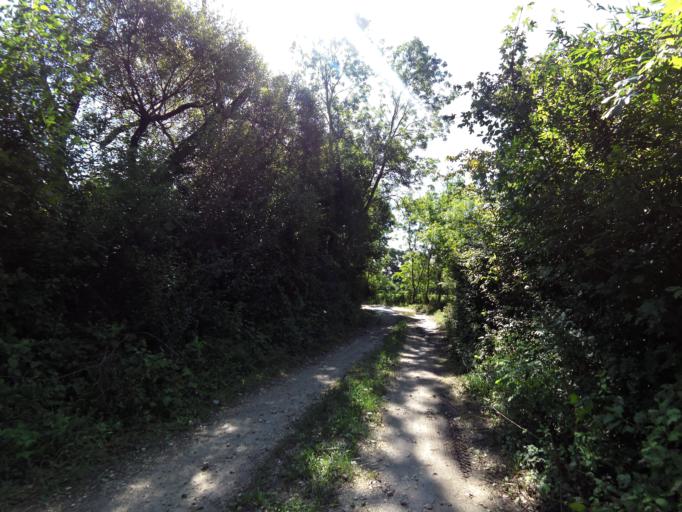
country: HU
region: Veszprem
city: Tapolca
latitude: 46.8340
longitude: 17.3999
